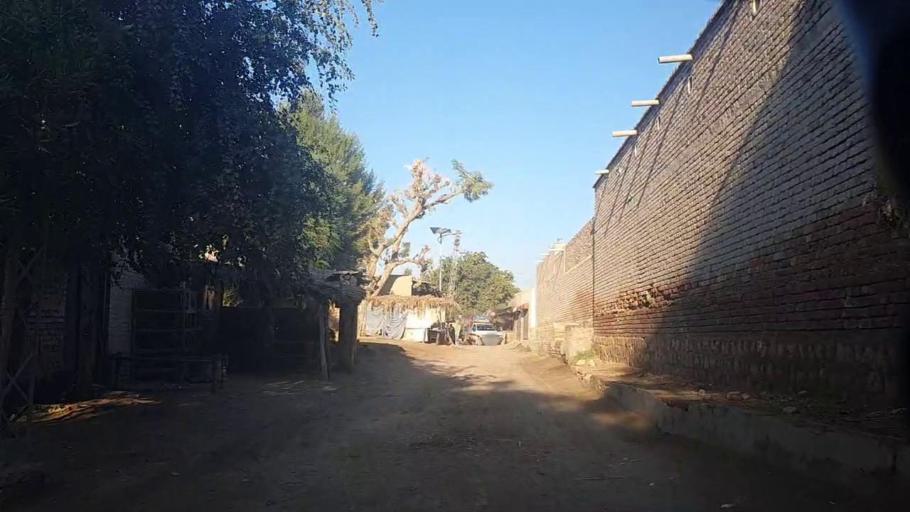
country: PK
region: Sindh
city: Sobhadero
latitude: 27.3970
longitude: 68.4201
